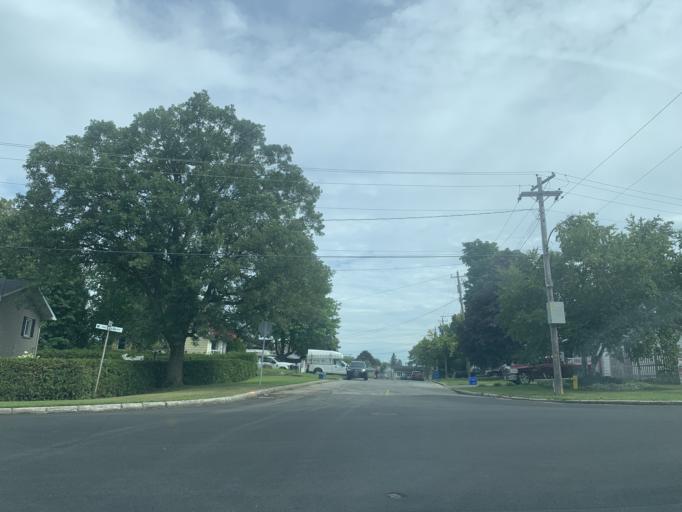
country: CA
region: Ontario
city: Hawkesbury
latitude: 45.6038
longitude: -74.6096
